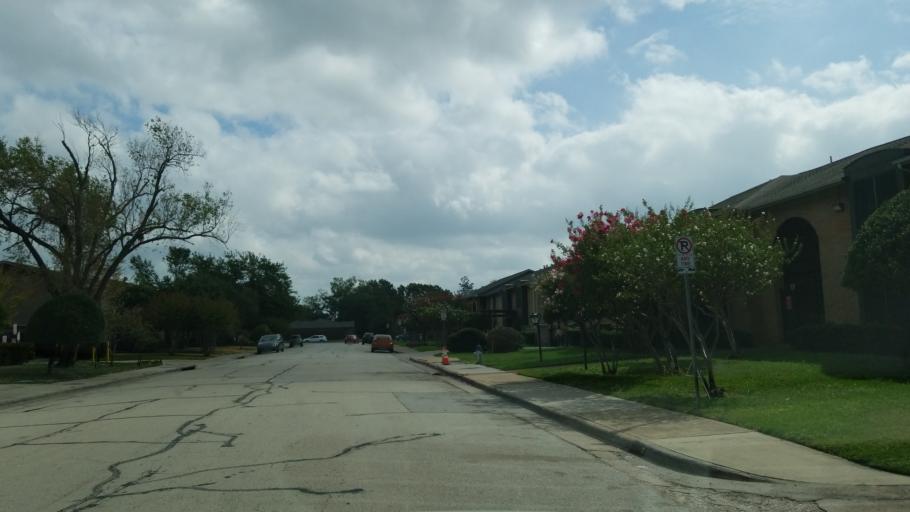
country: US
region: Texas
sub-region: Dallas County
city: Richardson
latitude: 32.9458
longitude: -96.7705
